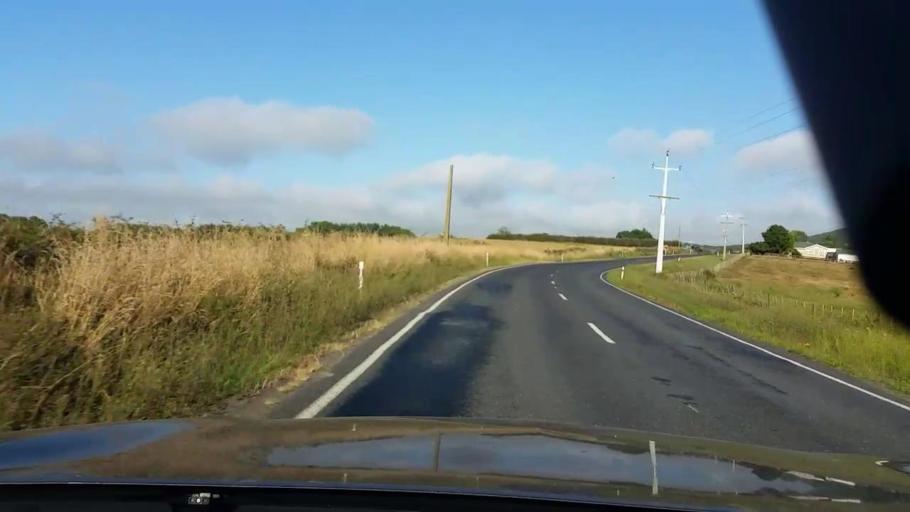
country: NZ
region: Waikato
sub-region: Hamilton City
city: Hamilton
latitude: -37.5922
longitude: 175.3811
